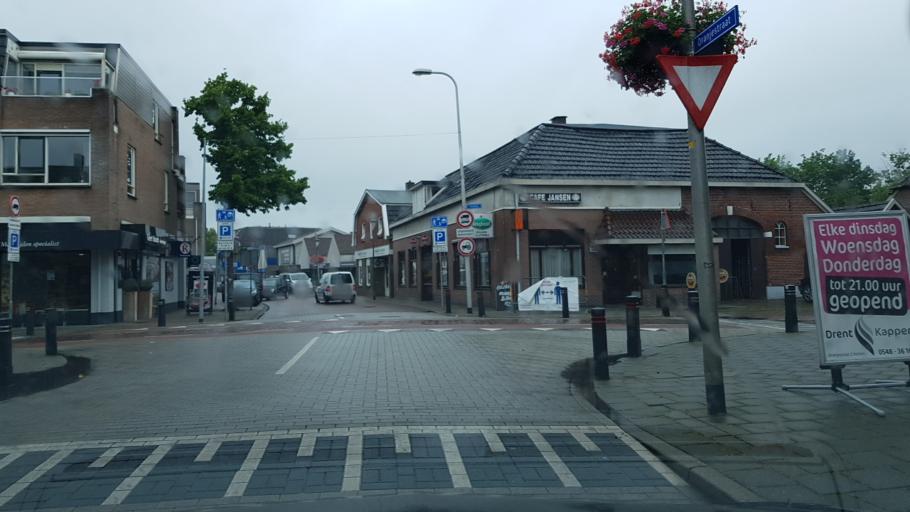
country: NL
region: Overijssel
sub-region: Gemeente Hof van Twente
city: Markelo
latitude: 52.2811
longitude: 6.4234
